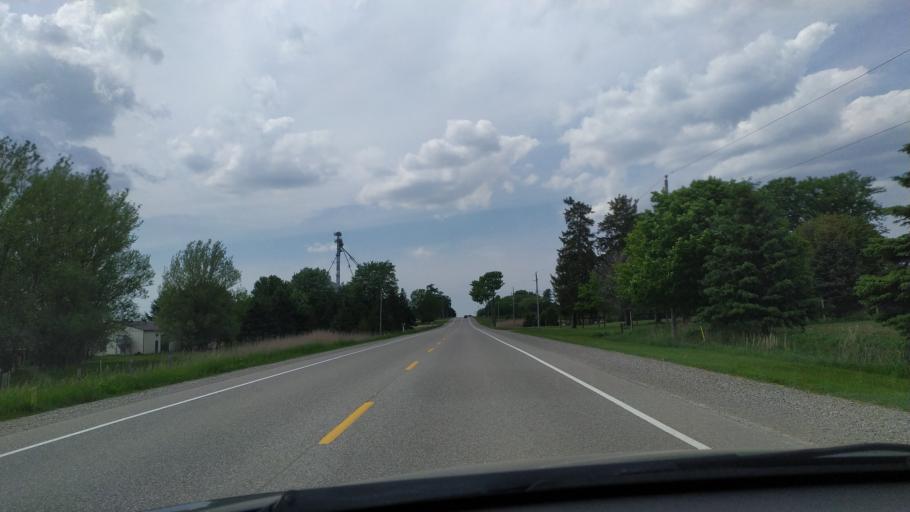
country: CA
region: Ontario
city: Dorchester
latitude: 43.1667
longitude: -81.0442
